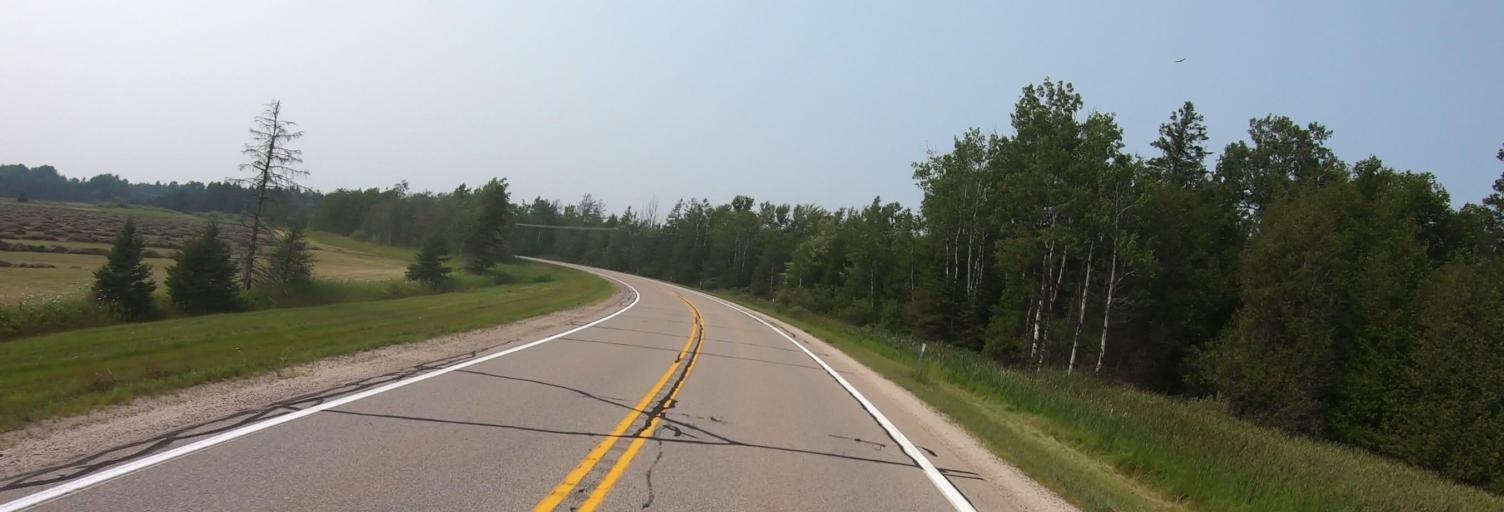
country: US
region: Michigan
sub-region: Chippewa County
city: Sault Ste. Marie
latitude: 46.1281
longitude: -84.2603
